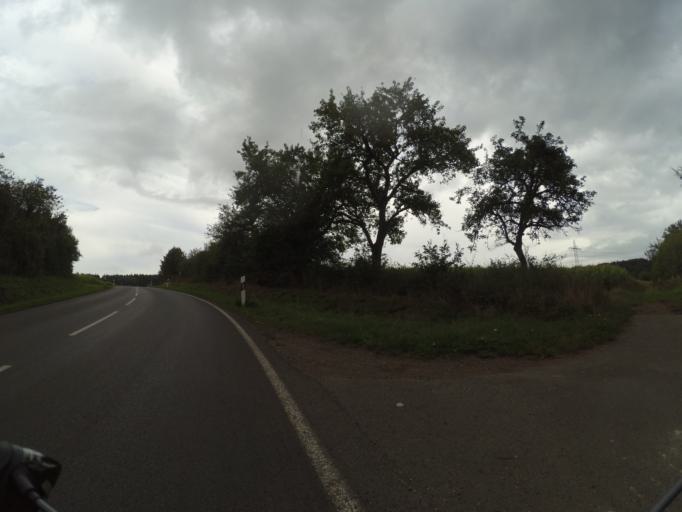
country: DE
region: Rheinland-Pfalz
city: Orenhofen
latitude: 49.9126
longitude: 6.6535
